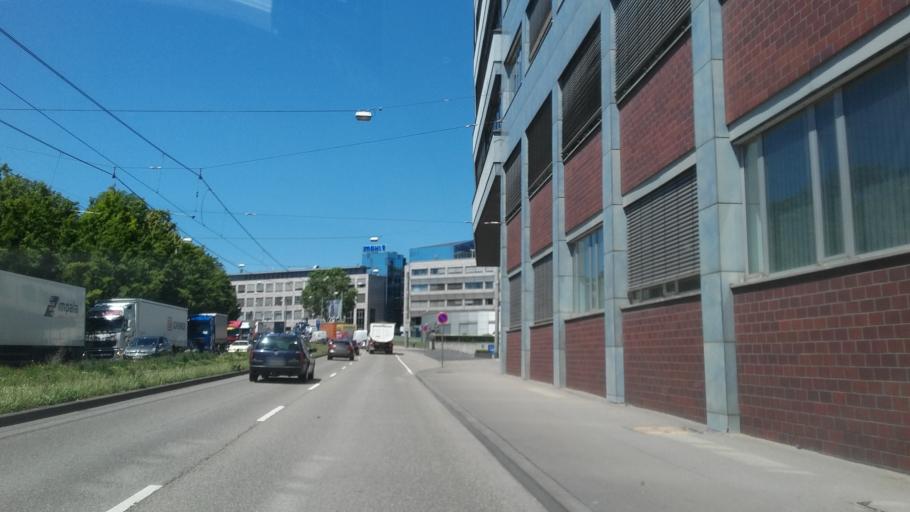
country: DE
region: Baden-Wuerttemberg
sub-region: Regierungsbezirk Stuttgart
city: Stuttgart-Ost
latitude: 48.8072
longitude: 9.2078
